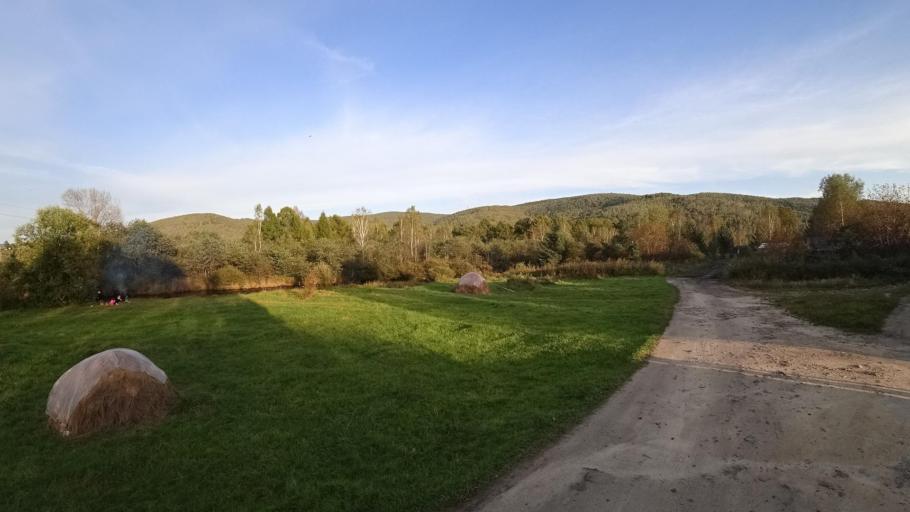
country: RU
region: Jewish Autonomous Oblast
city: Kul'dur
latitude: 49.1990
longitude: 131.6280
